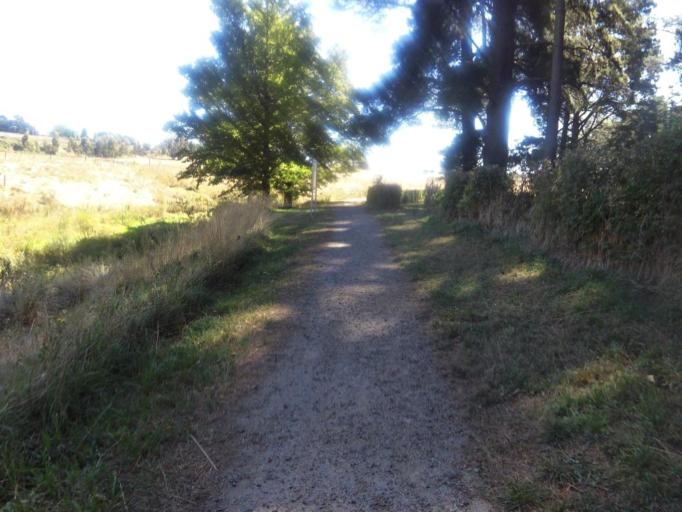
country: AU
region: Victoria
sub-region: Mount Alexander
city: Castlemaine
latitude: -37.2548
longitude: 144.4481
